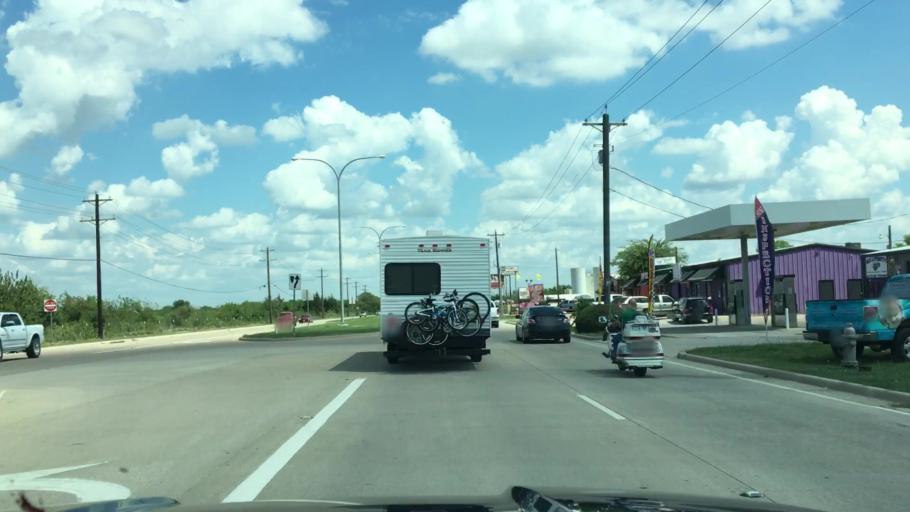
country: US
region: Texas
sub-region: Tarrant County
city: Keller
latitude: 32.9317
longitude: -97.3042
